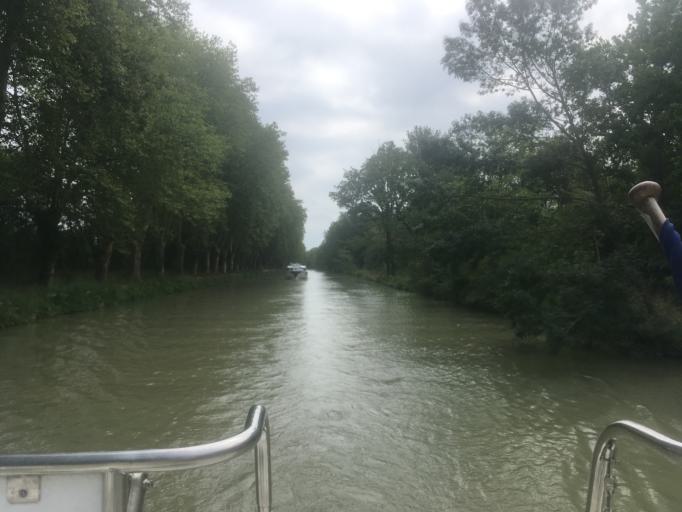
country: FR
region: Languedoc-Roussillon
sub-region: Departement de l'Aude
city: Villepinte
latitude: 43.2757
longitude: 2.0822
